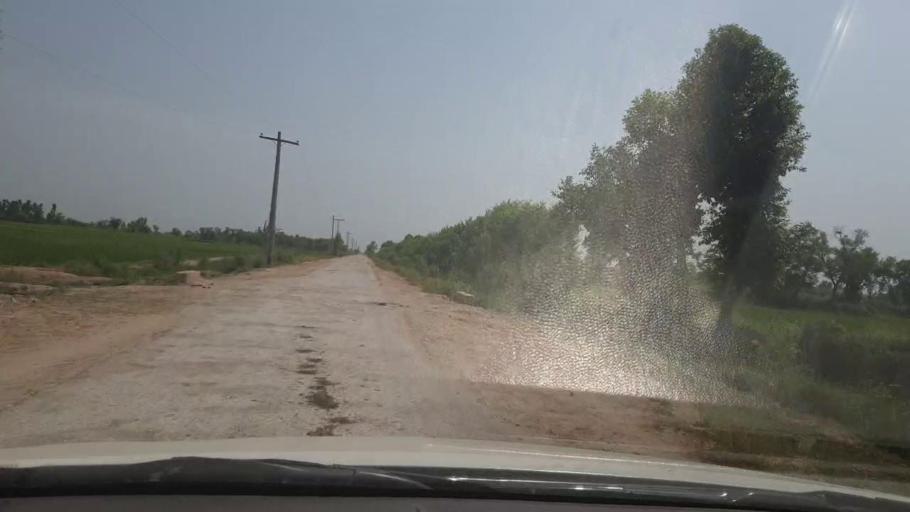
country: PK
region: Sindh
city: Garhi Yasin
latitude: 27.9737
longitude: 68.5034
